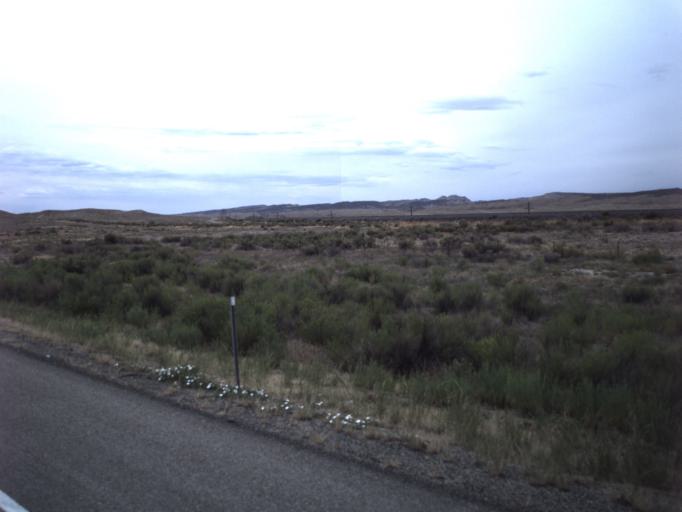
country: US
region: Utah
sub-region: Carbon County
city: East Carbon City
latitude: 39.2533
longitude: -110.3391
